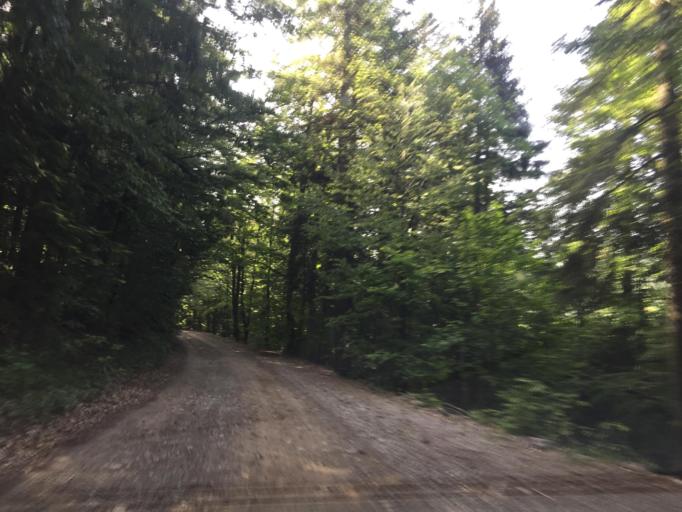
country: HR
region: Primorsko-Goranska
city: Klana
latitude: 45.4933
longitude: 14.4542
